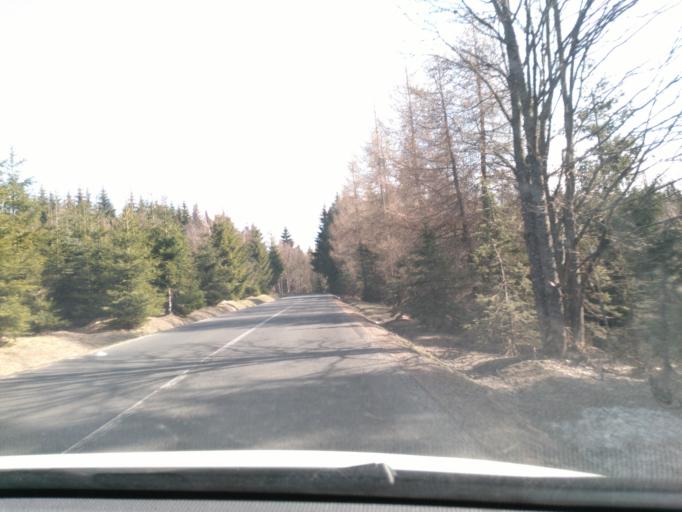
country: CZ
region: Ustecky
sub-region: Okres Chomutov
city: Kovarska
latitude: 50.4545
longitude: 13.0546
